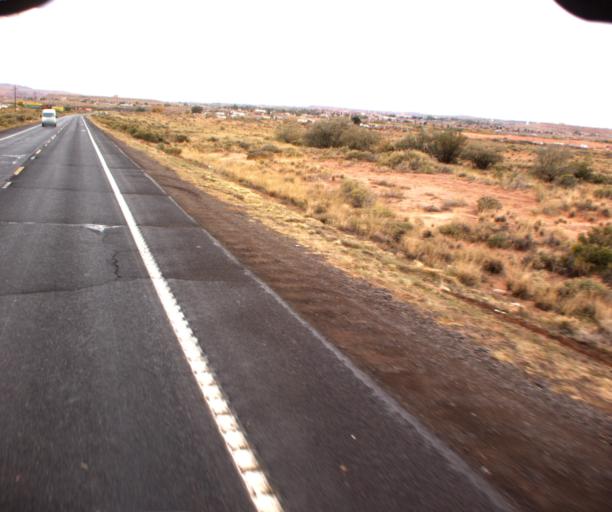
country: US
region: Arizona
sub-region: Coconino County
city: Tuba City
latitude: 36.1278
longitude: -111.1957
